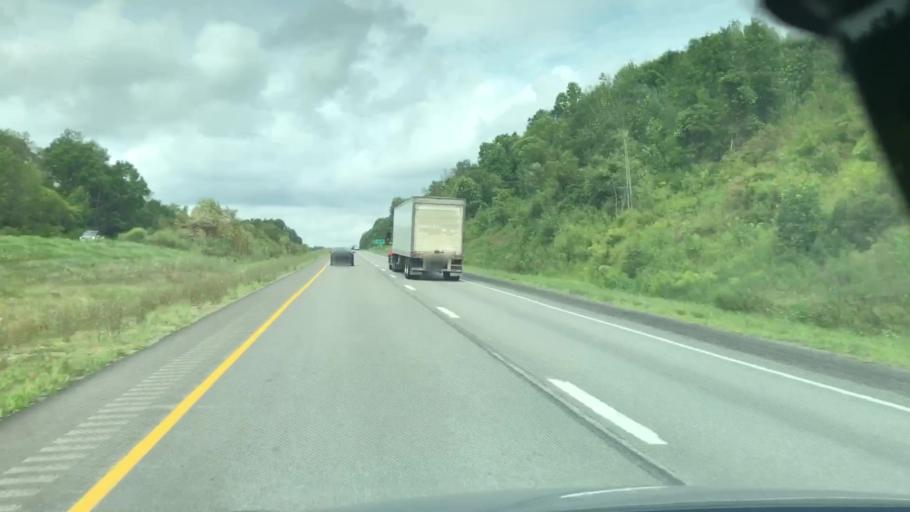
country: US
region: Pennsylvania
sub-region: Crawford County
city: Meadville
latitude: 41.5554
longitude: -80.1808
